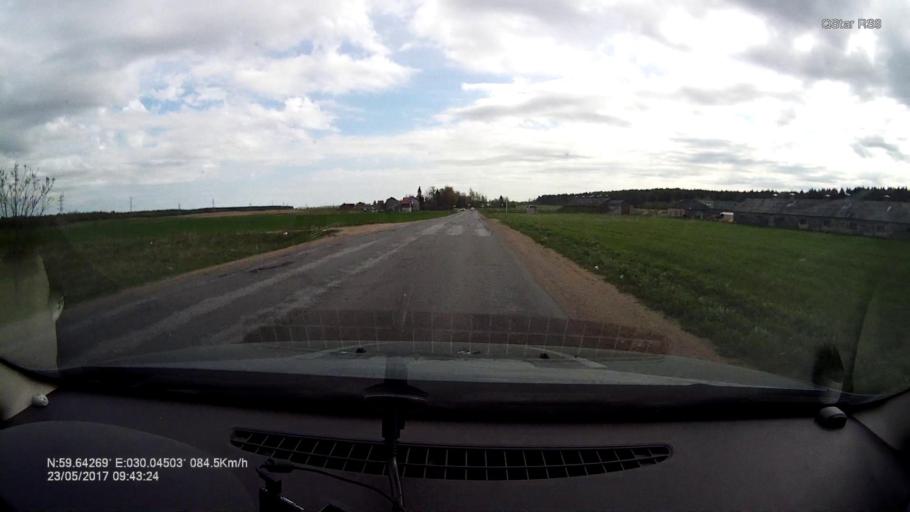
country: RU
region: Leningrad
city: Taytsy
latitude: 59.6428
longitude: 30.0456
